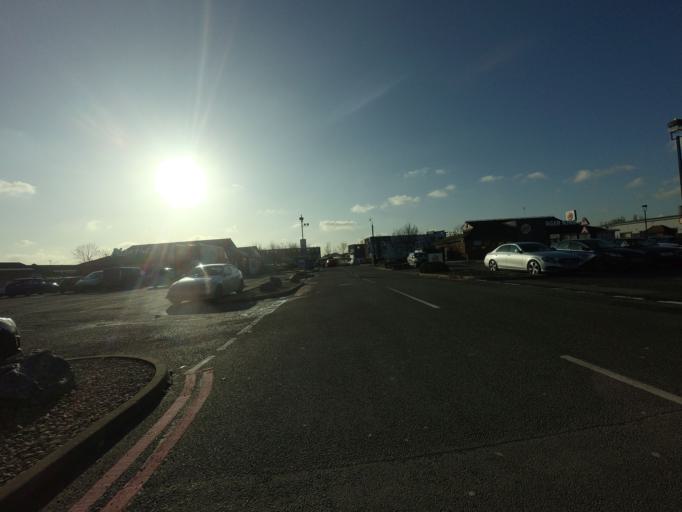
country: GB
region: England
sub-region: Greater London
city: Feltham
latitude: 51.4433
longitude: -0.4049
